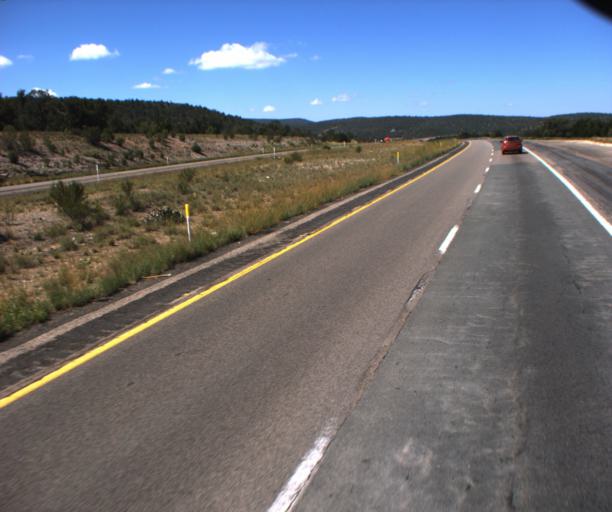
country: US
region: Arizona
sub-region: Mohave County
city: Peach Springs
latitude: 35.3006
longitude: -113.0208
